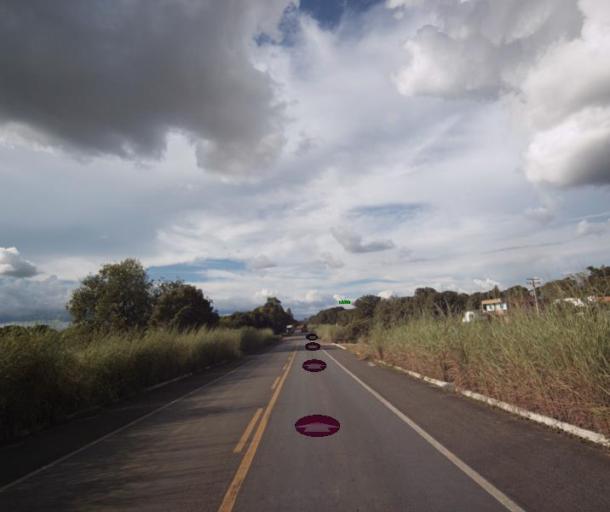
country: BR
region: Goias
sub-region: Niquelandia
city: Niquelandia
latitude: -14.7735
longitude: -48.6265
